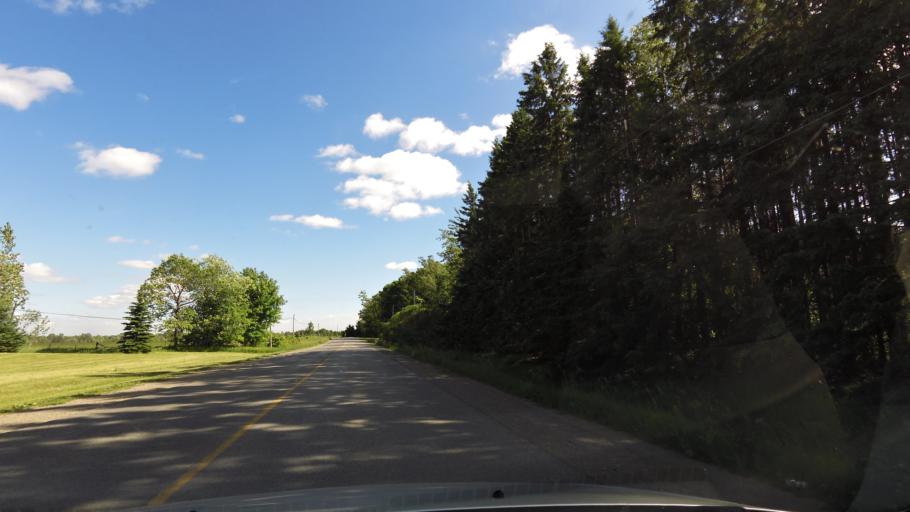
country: CA
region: Ontario
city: Bradford West Gwillimbury
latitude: 44.1618
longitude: -79.6156
